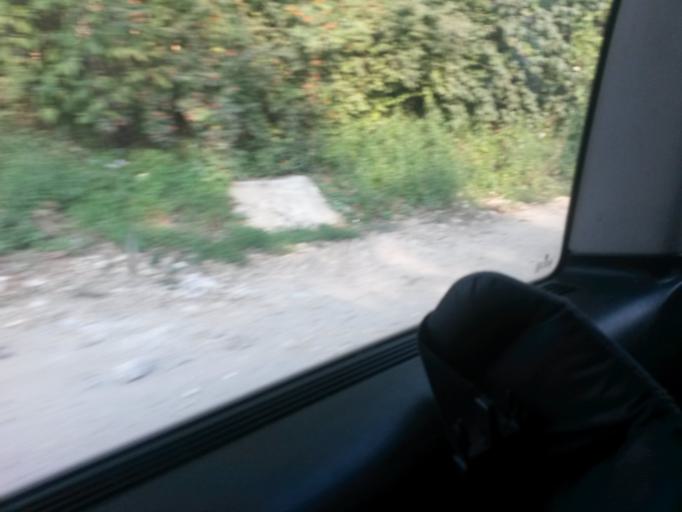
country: RO
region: Alba
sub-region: Municipiul Aiud
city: Aiudul de Sus
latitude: 46.3241
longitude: 23.6821
